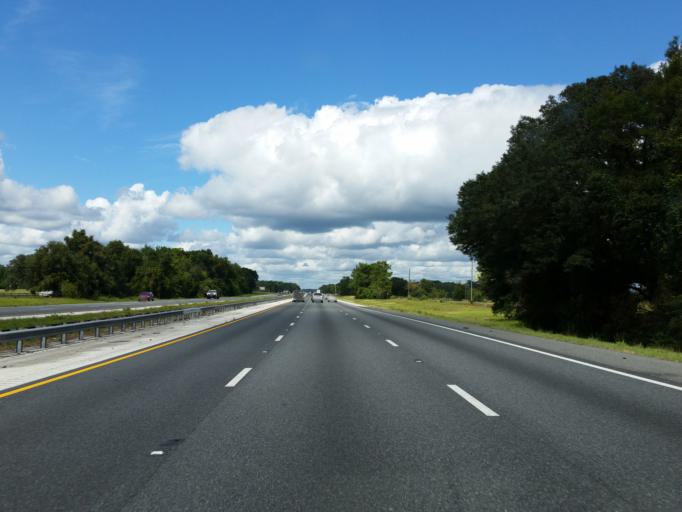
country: US
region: Florida
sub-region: Sumter County
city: Wildwood
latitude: 28.9407
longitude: -82.1134
